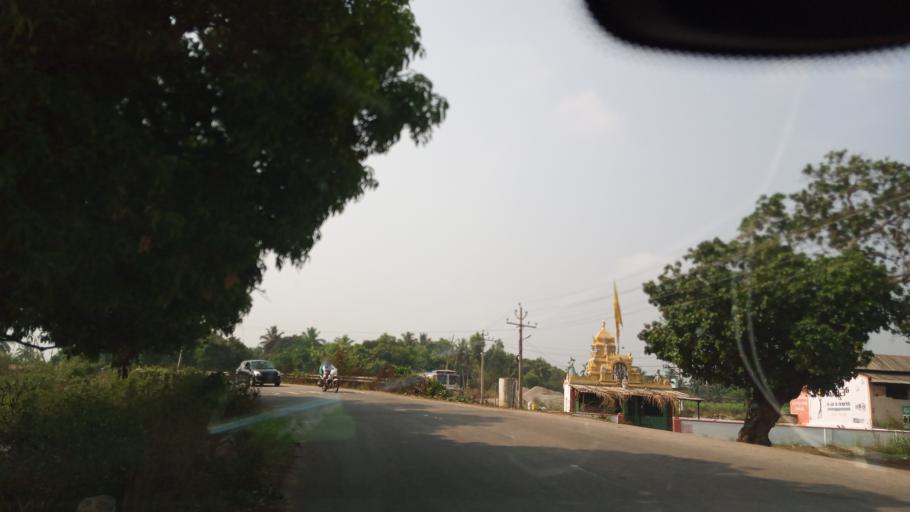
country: IN
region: Karnataka
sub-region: Mandya
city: Pandavapura
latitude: 12.5235
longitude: 76.6718
